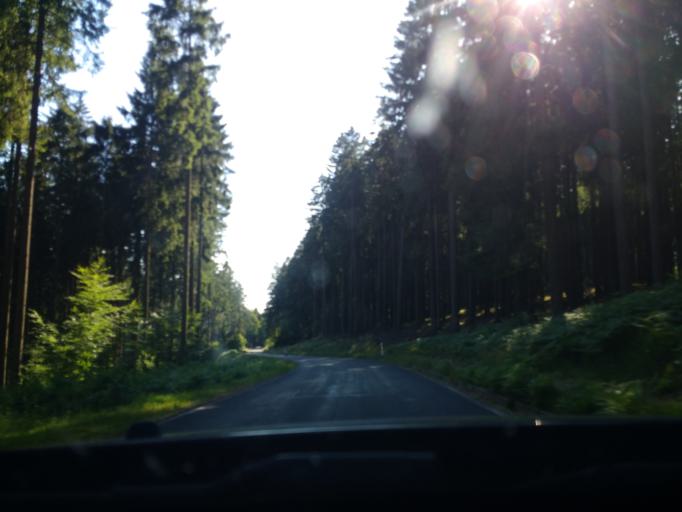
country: DE
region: Rheinland-Pfalz
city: Densborn
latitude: 50.1317
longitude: 6.6349
